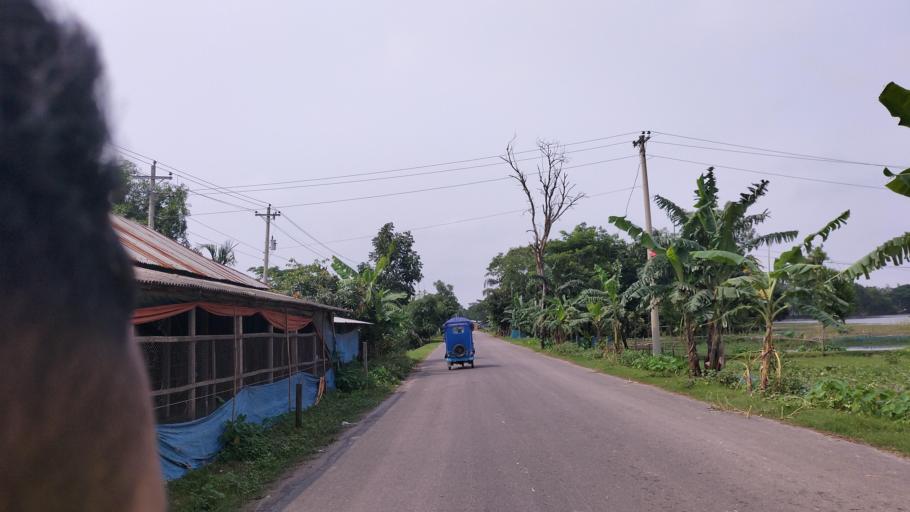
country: BD
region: Dhaka
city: Netrakona
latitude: 24.9490
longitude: 90.8322
